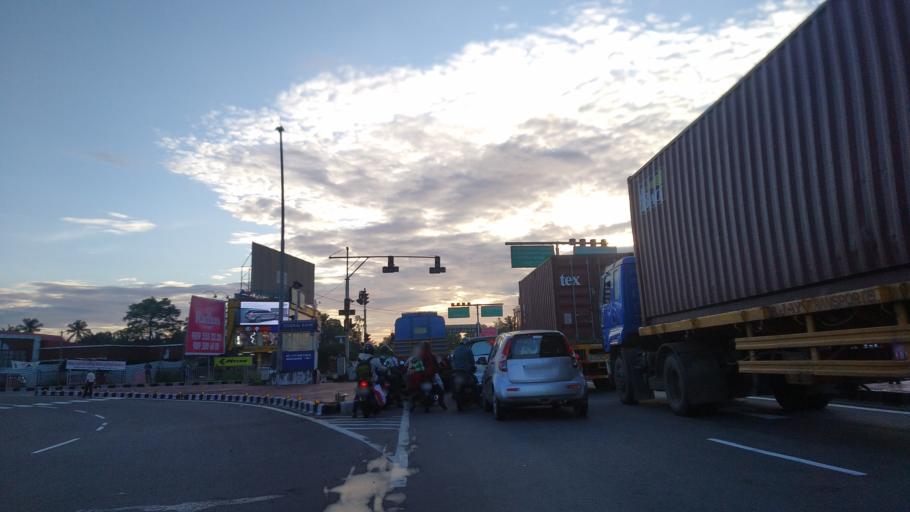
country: IN
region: Kerala
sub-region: Ernakulam
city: Elur
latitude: 10.0617
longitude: 76.2891
